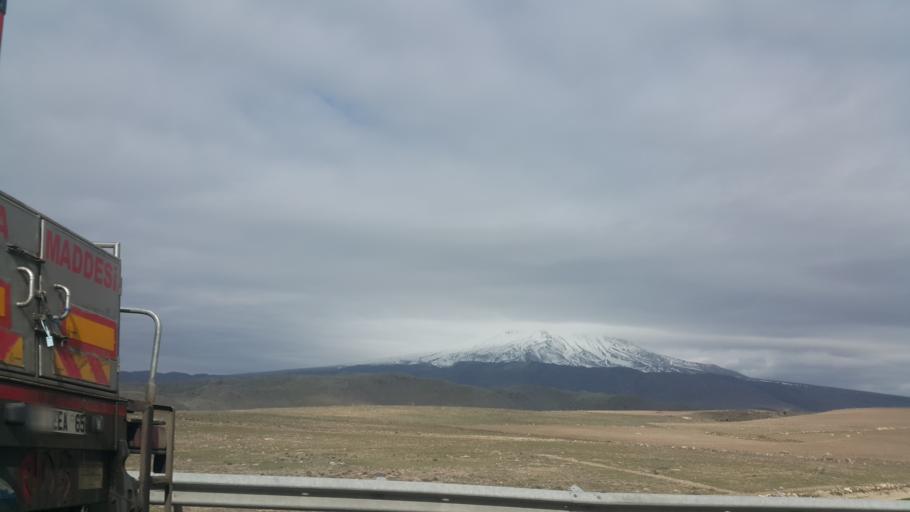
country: TR
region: Aksaray
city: Taspinar
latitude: 38.1435
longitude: 34.0347
